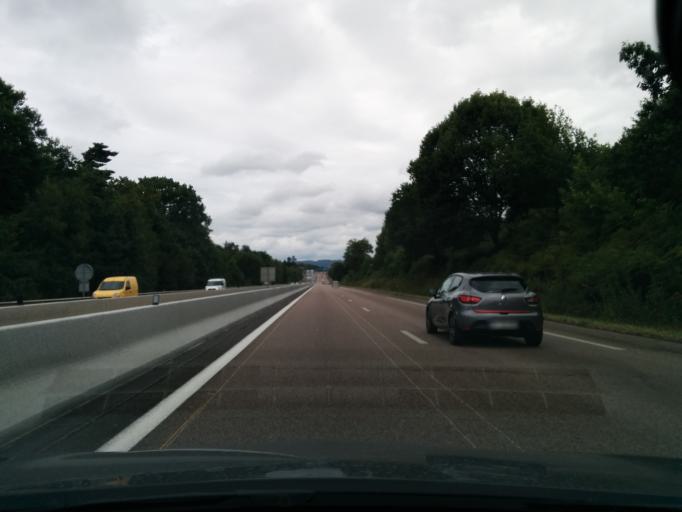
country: FR
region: Limousin
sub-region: Departement de la Haute-Vienne
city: Le Palais-sur-Vienne
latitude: 45.8685
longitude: 1.2876
